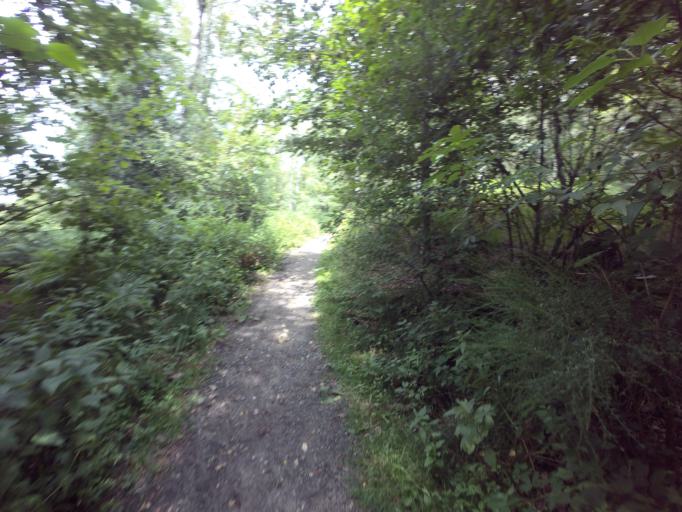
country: BE
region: Wallonia
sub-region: Province de Liege
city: Plombieres
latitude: 50.7586
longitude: 5.9747
